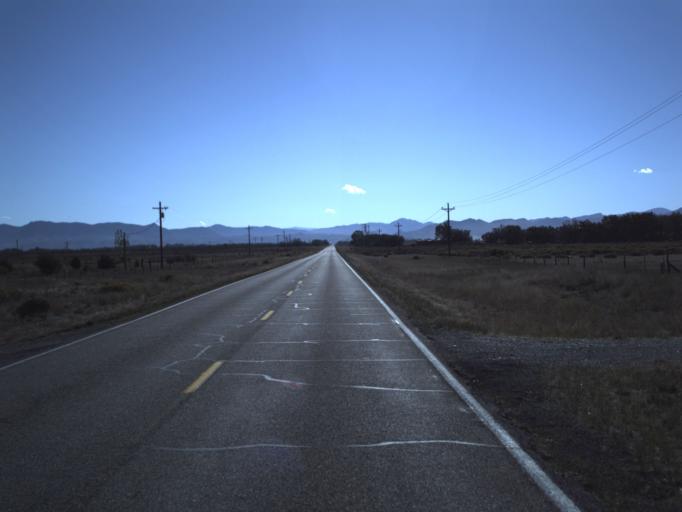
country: US
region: Utah
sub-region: Washington County
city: Enterprise
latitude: 37.7246
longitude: -113.6984
